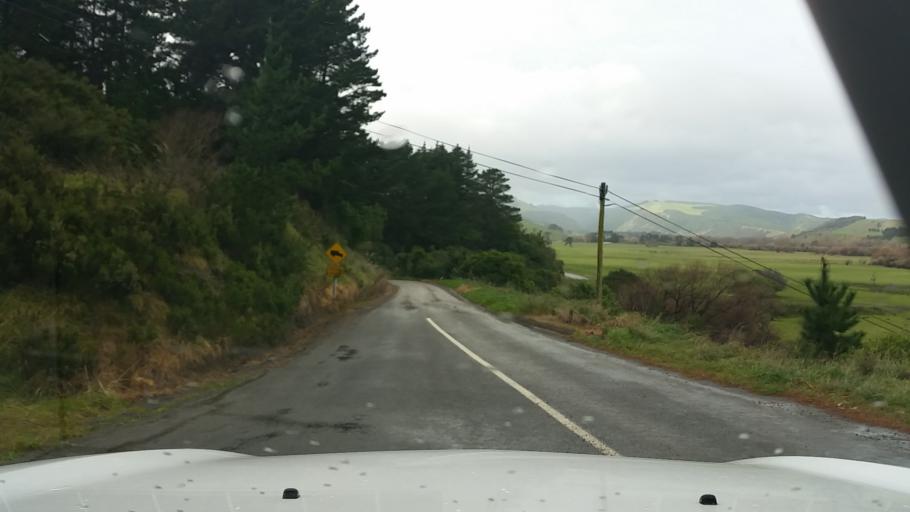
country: NZ
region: Wellington
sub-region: Upper Hutt City
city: Upper Hutt
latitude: -41.3653
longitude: 175.1986
